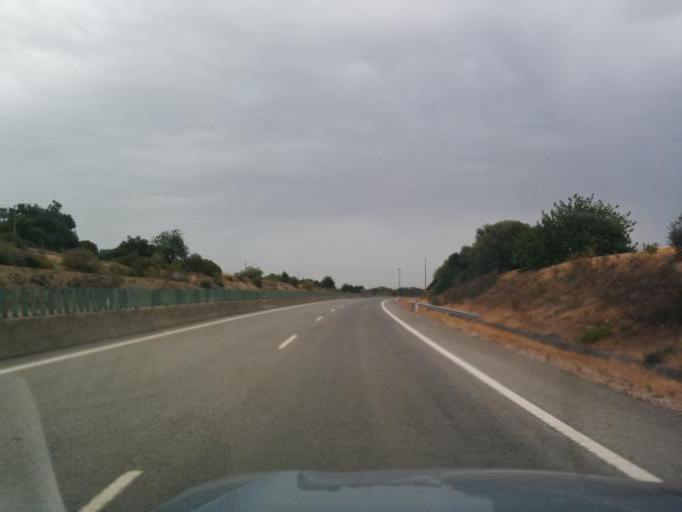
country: PT
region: Faro
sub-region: Tavira
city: Luz
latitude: 37.1373
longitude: -7.7330
